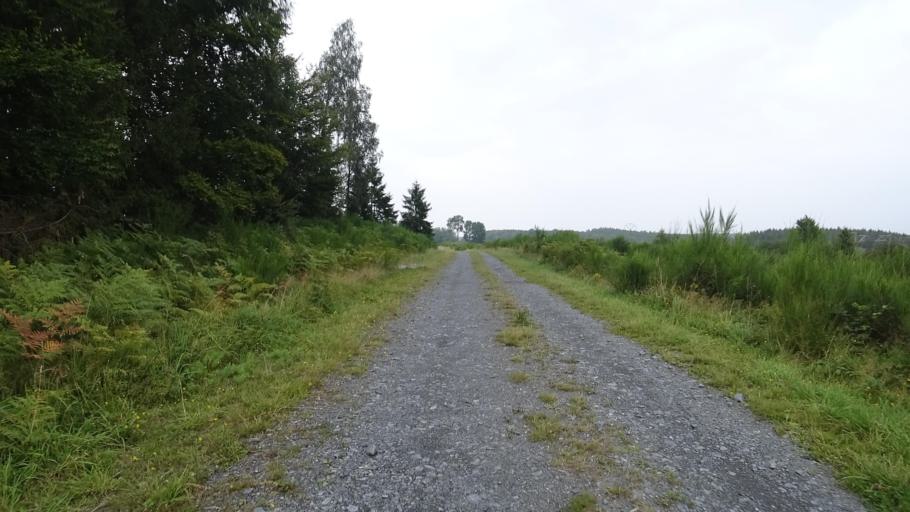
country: BE
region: Wallonia
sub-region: Province du Luxembourg
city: Chiny
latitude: 49.7909
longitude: 5.3262
